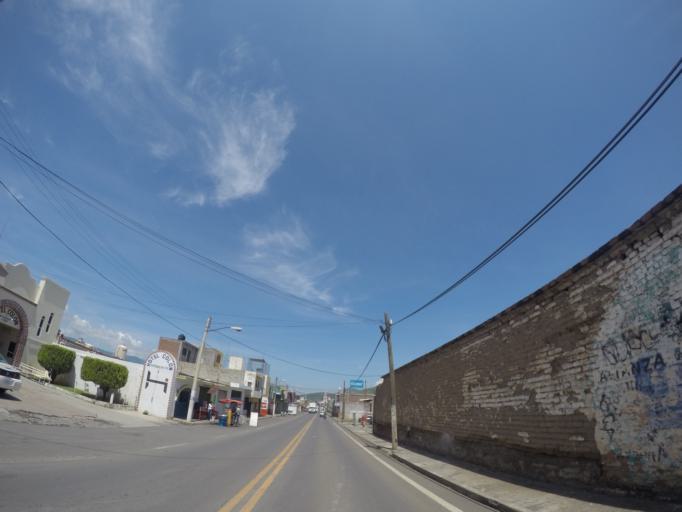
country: MX
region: Nayarit
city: Ixtlan del Rio
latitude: 21.0338
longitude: -104.3625
